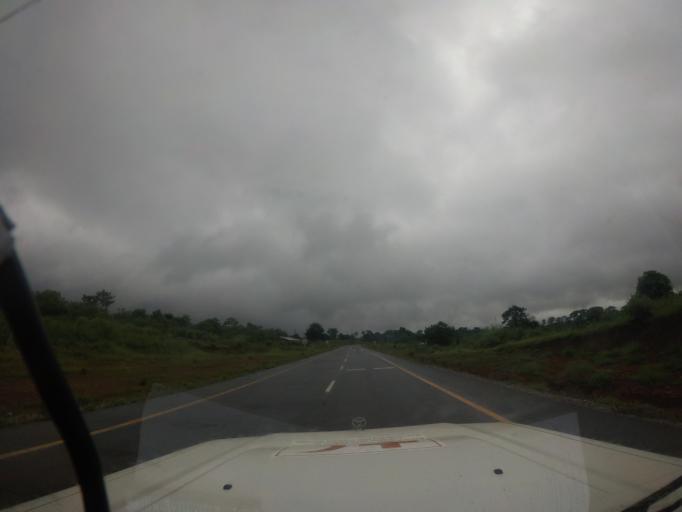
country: SL
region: Eastern Province
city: Hangha
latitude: 7.9333
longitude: -11.1473
